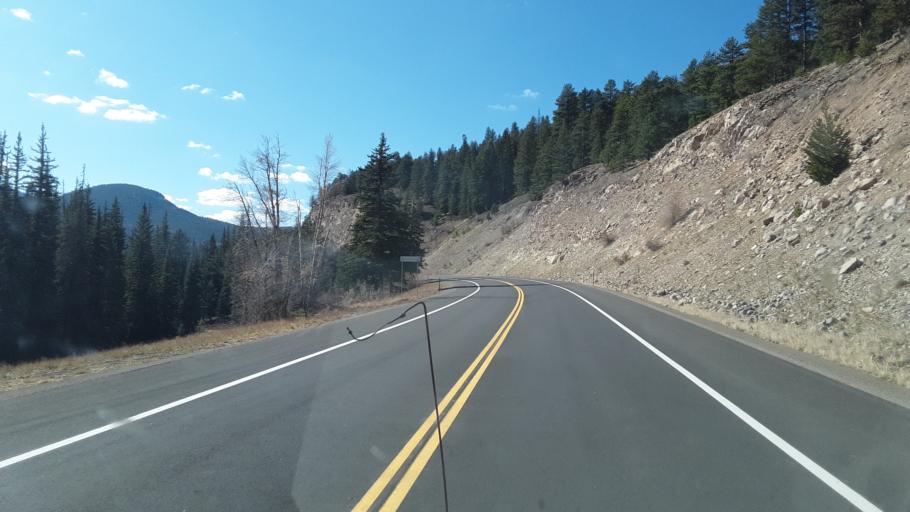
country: US
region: Colorado
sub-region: Rio Grande County
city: Del Norte
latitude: 37.6299
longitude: -106.6793
